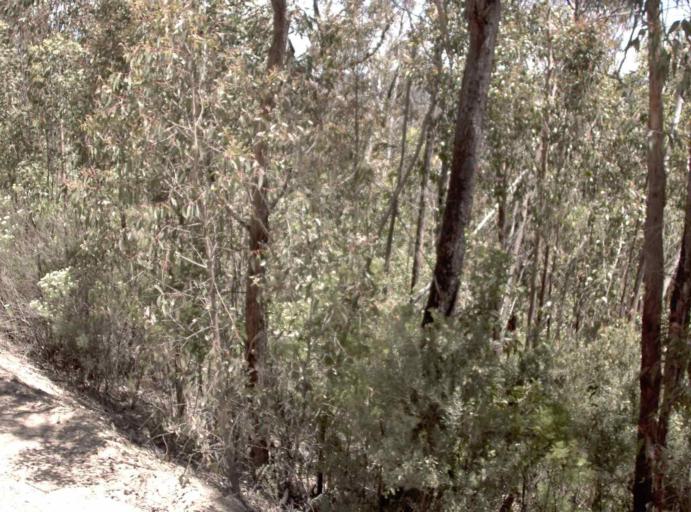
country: AU
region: New South Wales
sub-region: Snowy River
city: Jindabyne
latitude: -37.0880
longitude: 148.3271
